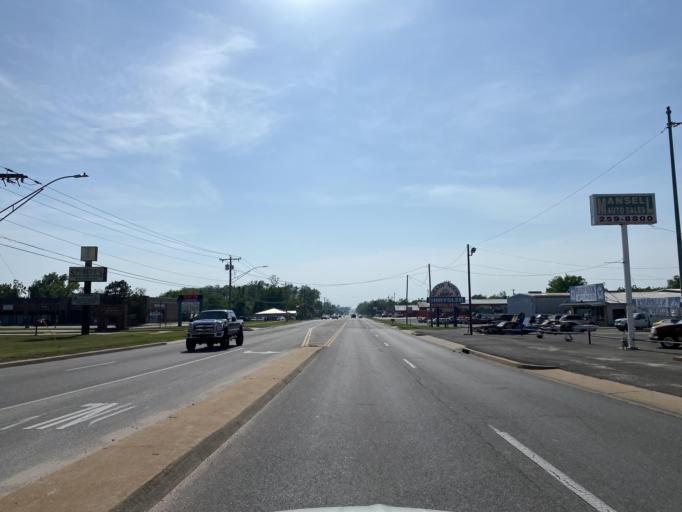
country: US
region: Oklahoma
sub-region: Oklahoma County
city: Nicoma Park
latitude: 35.4931
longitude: -97.3535
